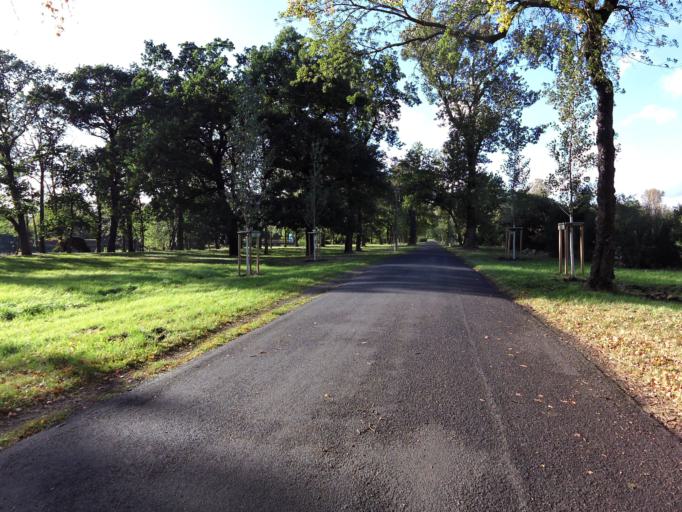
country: DE
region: Saxony-Anhalt
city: Magdeburg
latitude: 52.1186
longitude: 11.6465
